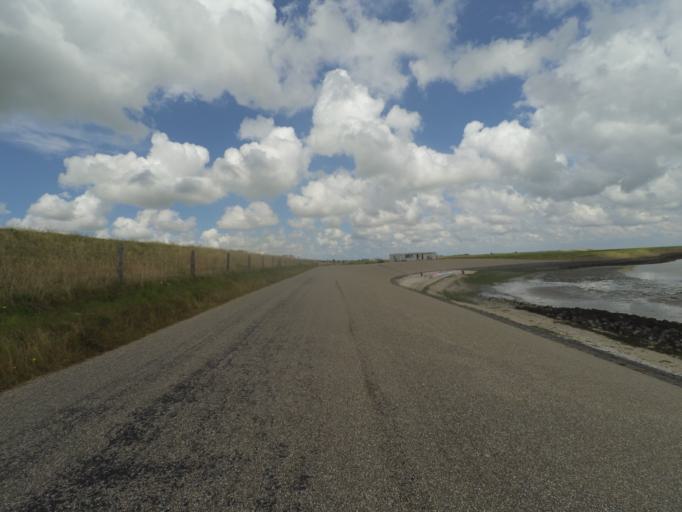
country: NL
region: North Holland
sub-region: Gemeente Texel
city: Den Burg
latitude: 53.0642
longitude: 4.8725
